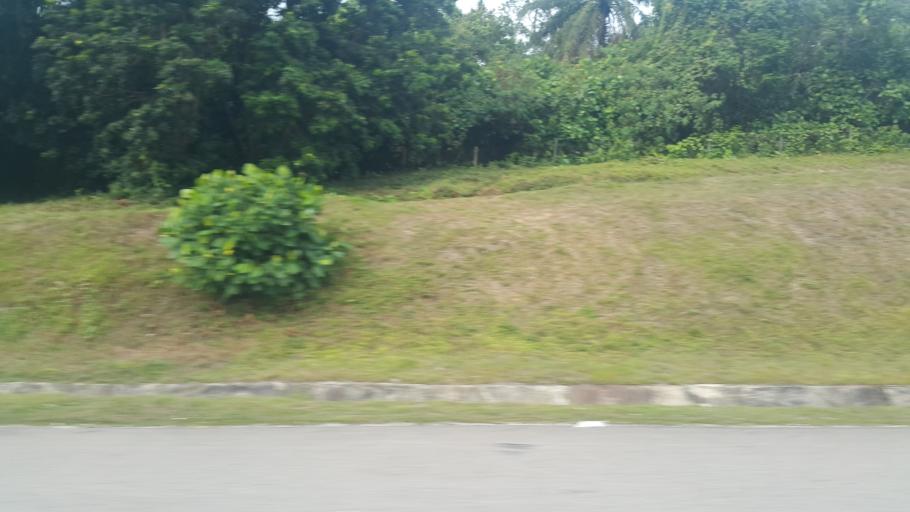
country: MY
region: Johor
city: Pekan Nenas
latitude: 1.3884
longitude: 103.5918
